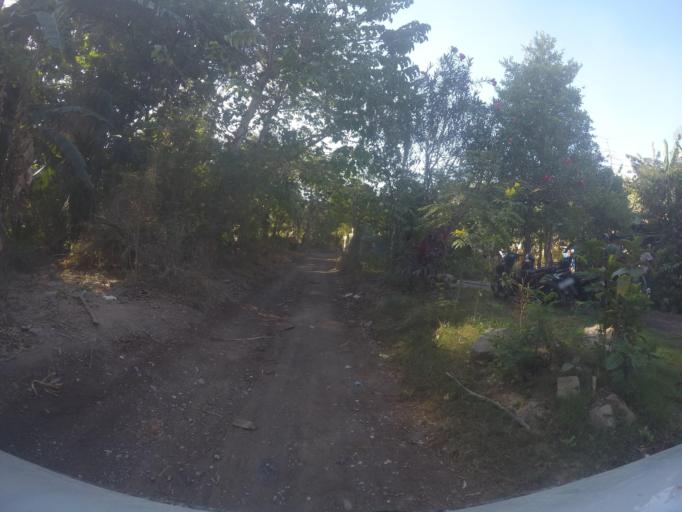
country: ID
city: Metinaro
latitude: -8.5420
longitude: 125.6652
